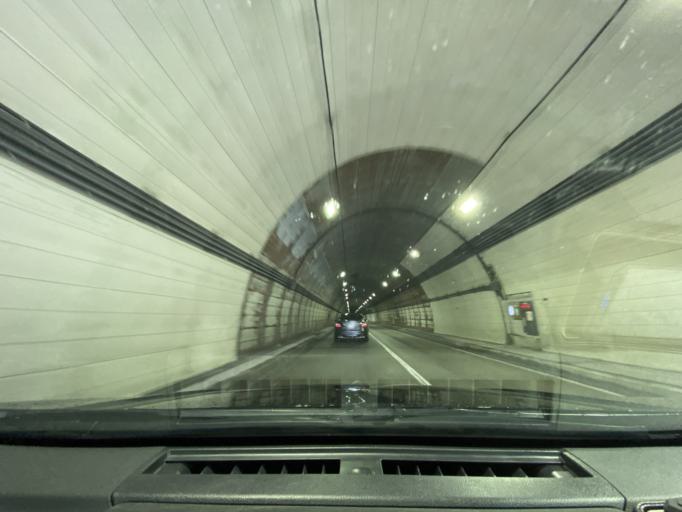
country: JP
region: Hokkaido
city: Ishikari
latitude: 43.4487
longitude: 141.4101
